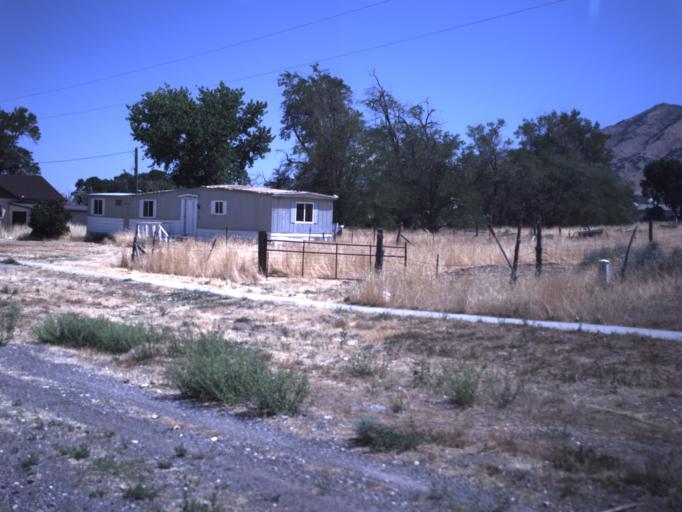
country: US
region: Utah
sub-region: Millard County
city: Delta
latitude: 39.3700
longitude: -112.3361
